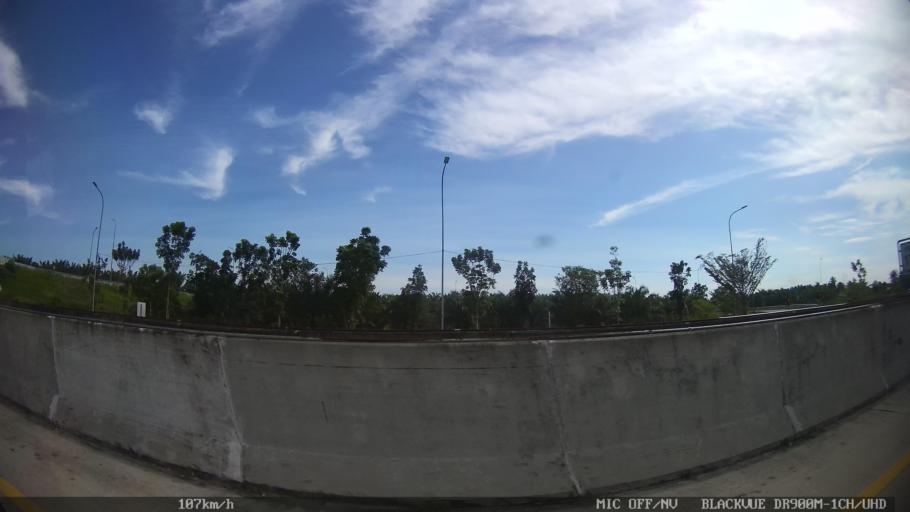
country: ID
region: North Sumatra
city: Binjai
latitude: 3.6469
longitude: 98.5489
